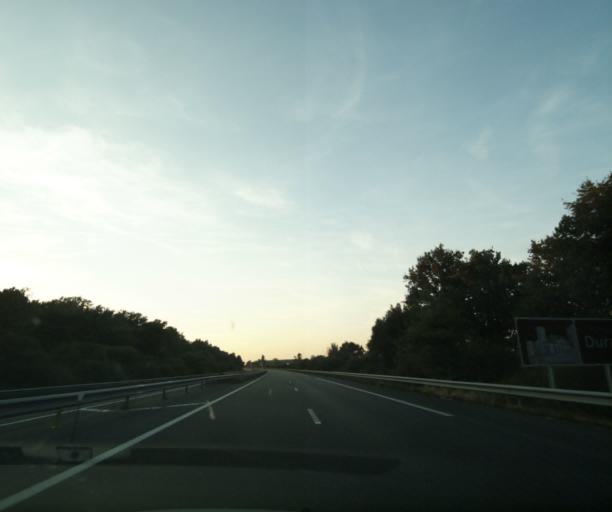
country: FR
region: Aquitaine
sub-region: Departement du Lot-et-Garonne
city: Fourques-sur-Garonne
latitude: 44.4192
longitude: 0.1730
